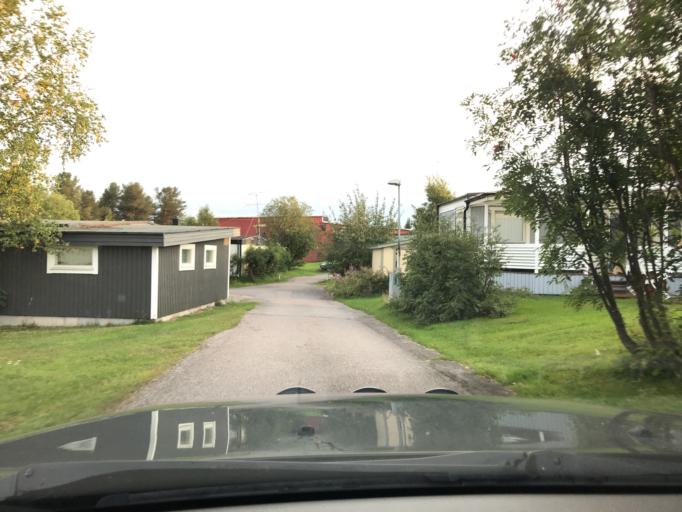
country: SE
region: Norrbotten
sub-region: Gallivare Kommun
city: Malmberget
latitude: 67.6485
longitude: 21.0530
